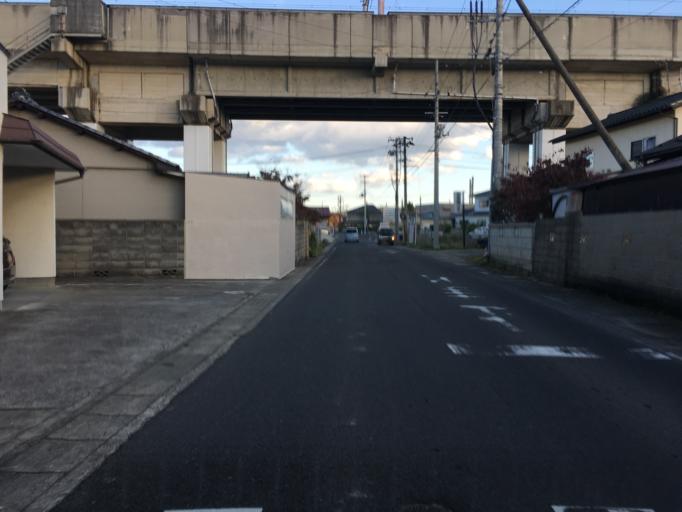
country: JP
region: Fukushima
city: Fukushima-shi
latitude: 37.8069
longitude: 140.4819
